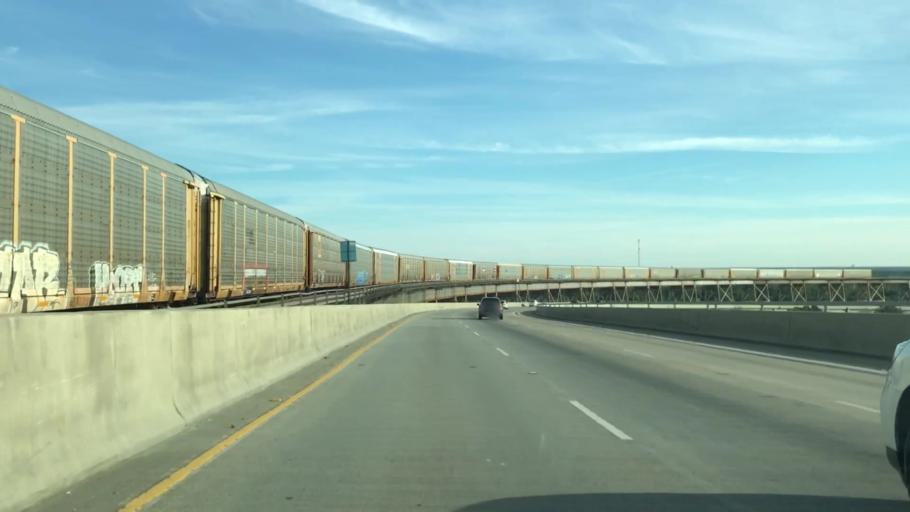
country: US
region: Louisiana
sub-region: Jefferson Parish
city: Bridge City
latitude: 29.9408
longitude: -90.1653
